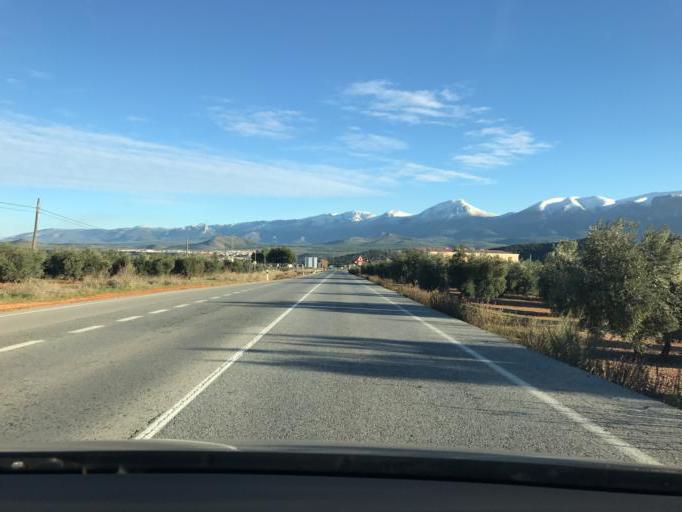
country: ES
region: Andalusia
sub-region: Provincia de Granada
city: Iznalloz
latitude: 37.4026
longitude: -3.5581
